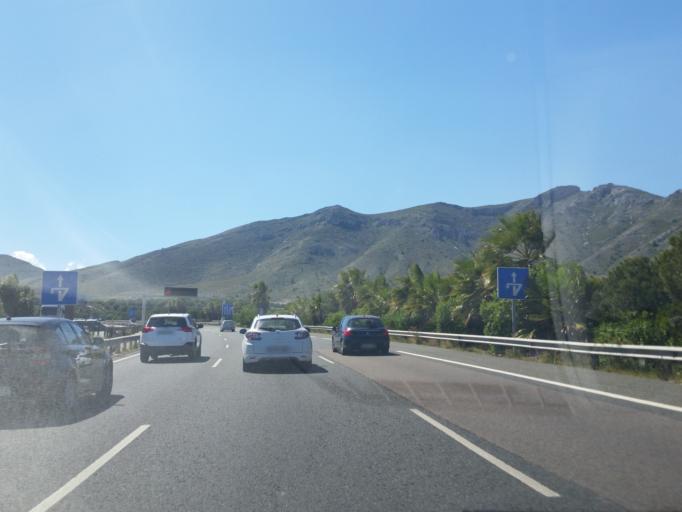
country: ES
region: Andalusia
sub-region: Provincia de Malaga
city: Torremolinos
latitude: 36.6429
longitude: -4.5048
